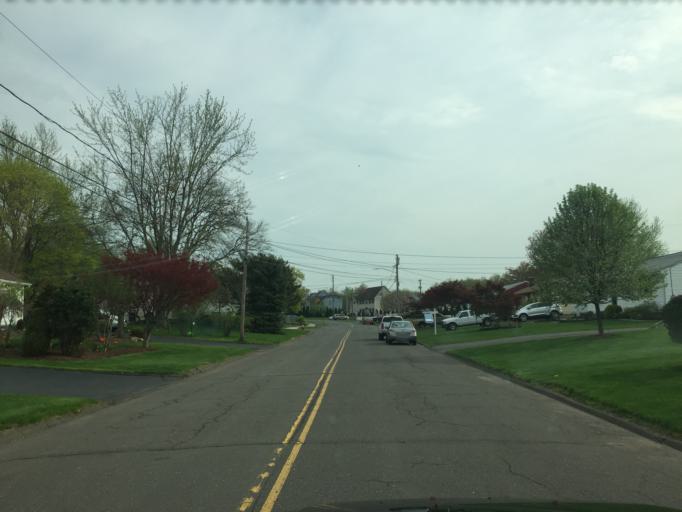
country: US
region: Connecticut
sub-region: Hartford County
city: Newington
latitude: 41.6969
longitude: -72.7451
